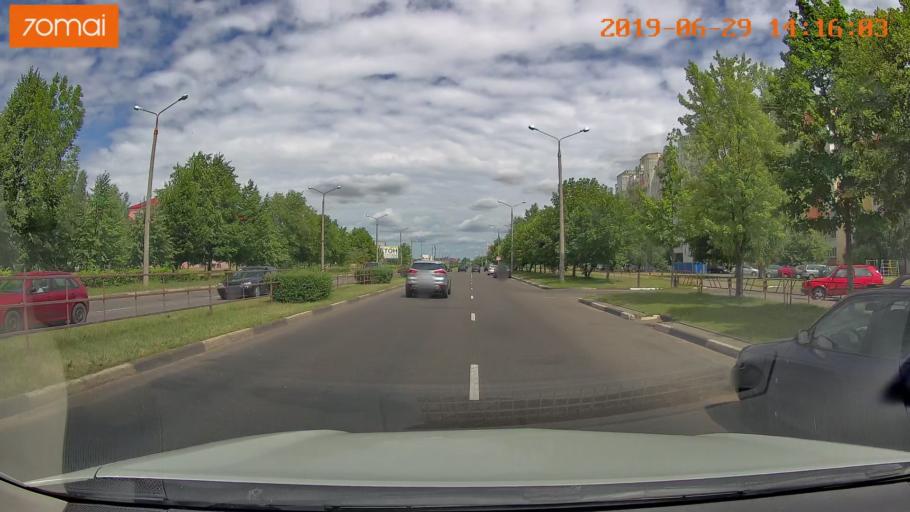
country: BY
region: Minsk
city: Salihorsk
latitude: 52.7941
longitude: 27.5280
